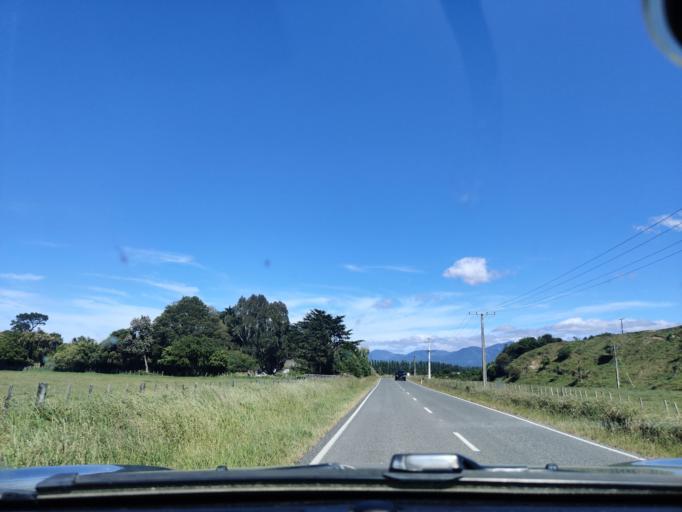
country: NZ
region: Wellington
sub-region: Upper Hutt City
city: Upper Hutt
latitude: -41.3668
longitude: 175.1917
